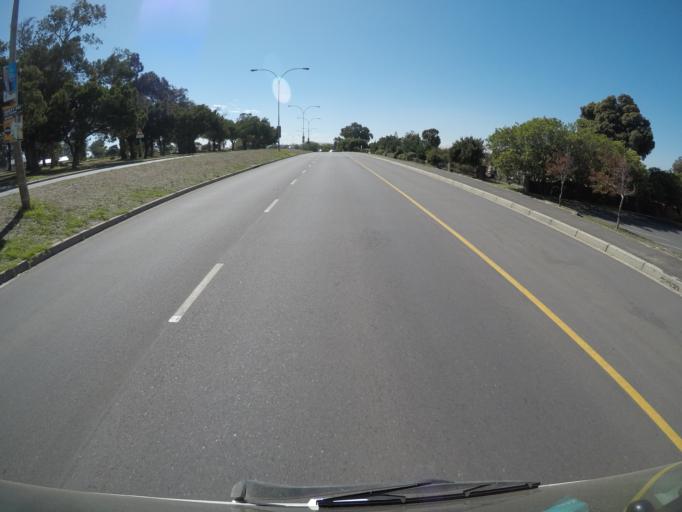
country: ZA
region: Western Cape
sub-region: City of Cape Town
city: Kraaifontein
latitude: -33.8389
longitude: 18.6489
